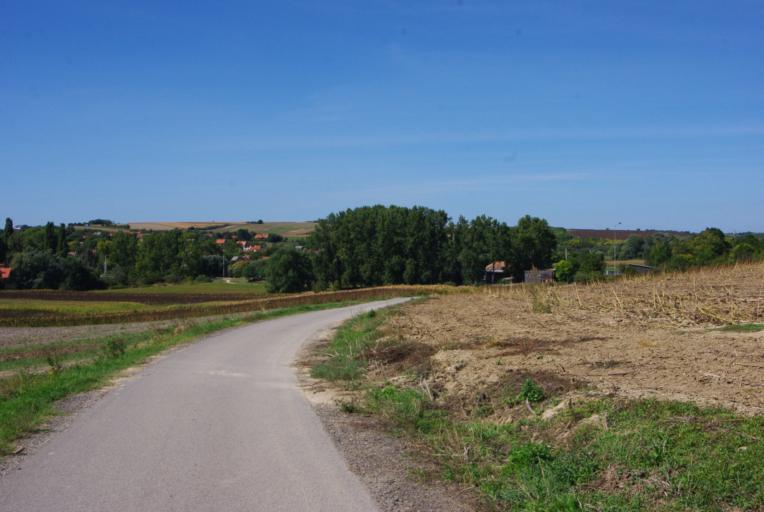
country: HU
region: Pest
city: Perbal
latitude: 47.5902
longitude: 18.7722
